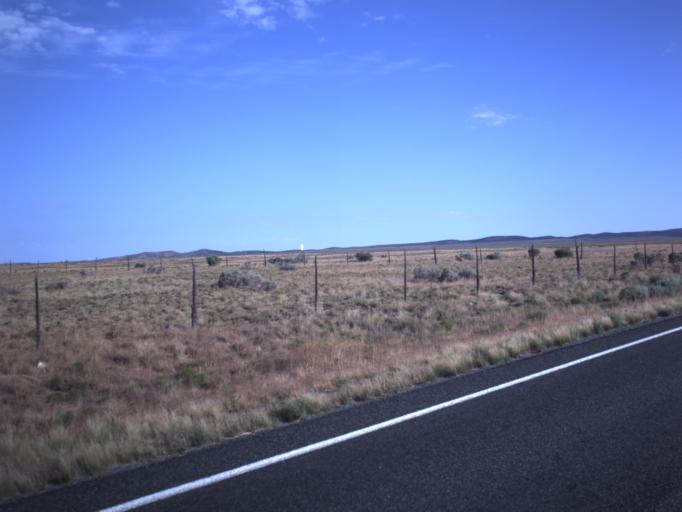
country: US
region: Utah
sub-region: Iron County
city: Enoch
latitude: 37.9027
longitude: -113.0315
